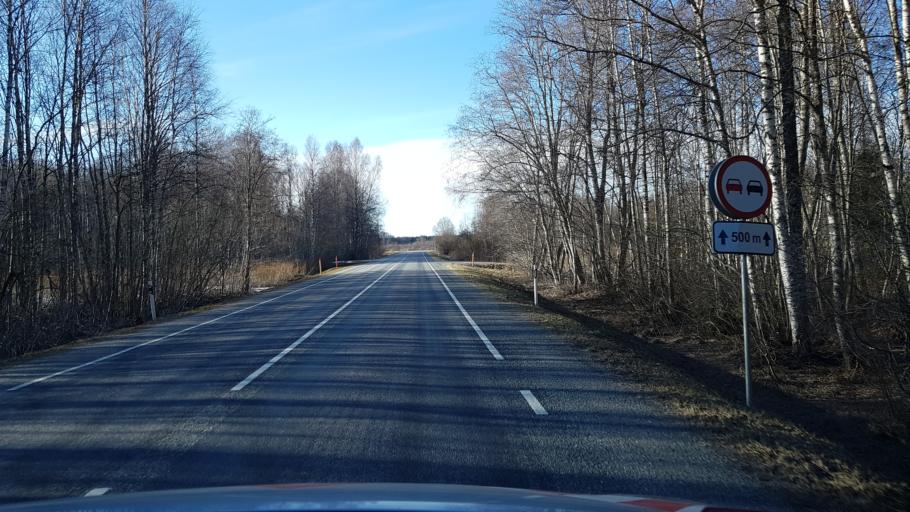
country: EE
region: Laeaene-Virumaa
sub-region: Tapa vald
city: Tapa
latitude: 59.4428
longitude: 25.9542
